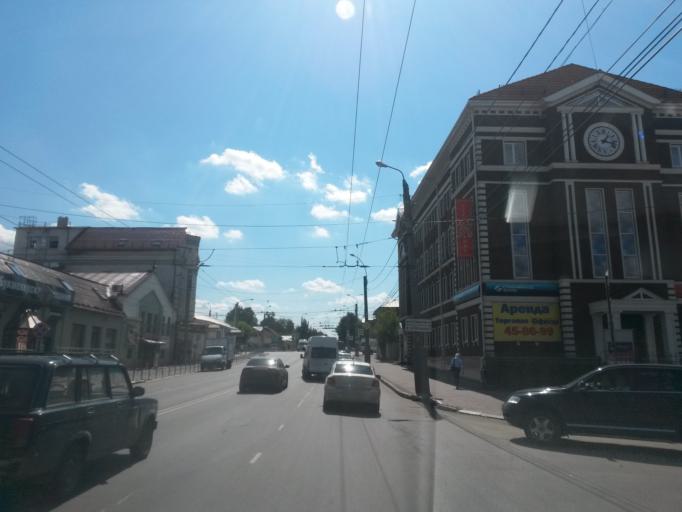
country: RU
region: Ivanovo
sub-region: Gorod Ivanovo
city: Ivanovo
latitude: 56.9935
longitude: 40.9867
